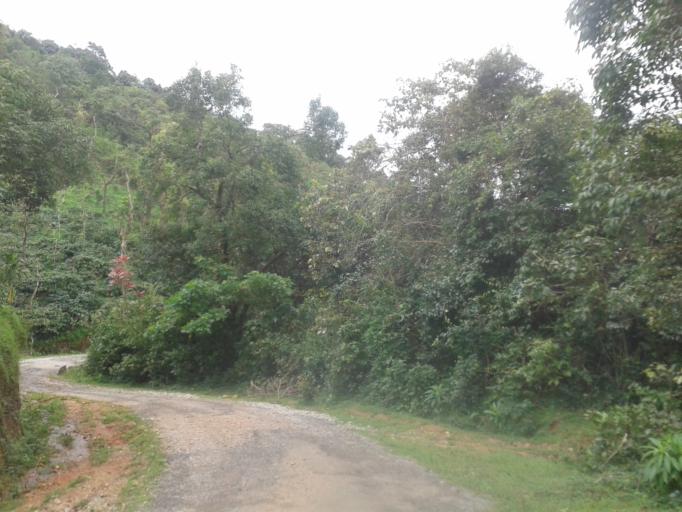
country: IN
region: Karnataka
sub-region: Chikmagalur
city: Mudigere
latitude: 12.9820
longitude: 75.6151
